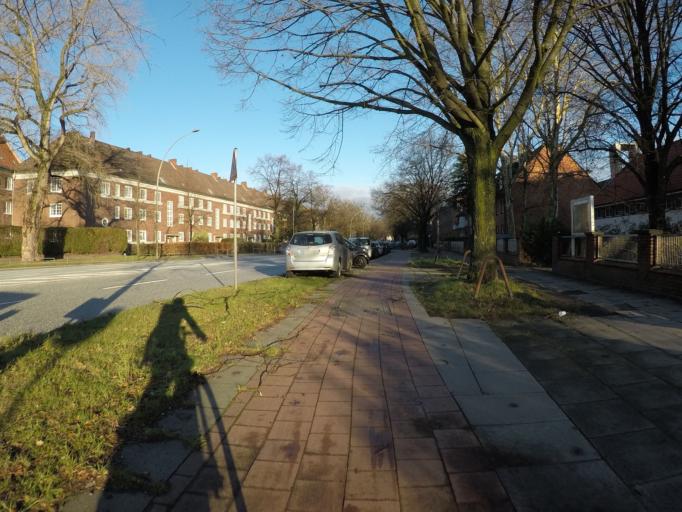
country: DE
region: Hamburg
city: Fuhlsbuettel
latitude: 53.6239
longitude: 10.0118
